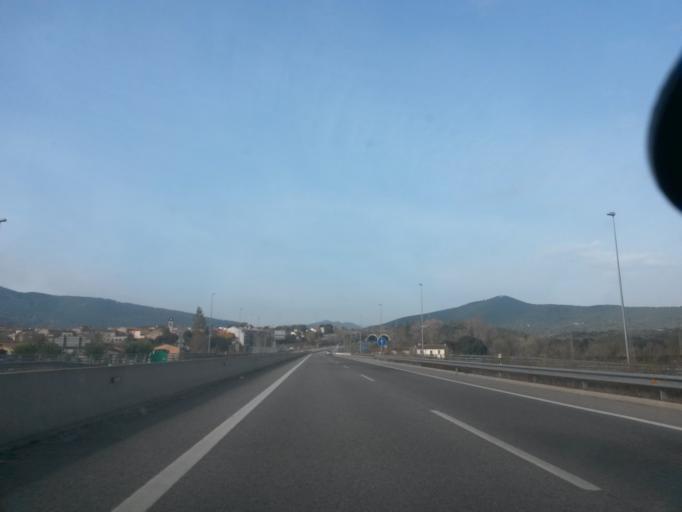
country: ES
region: Catalonia
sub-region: Provincia de Girona
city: Argelaguer
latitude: 42.2131
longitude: 2.6140
